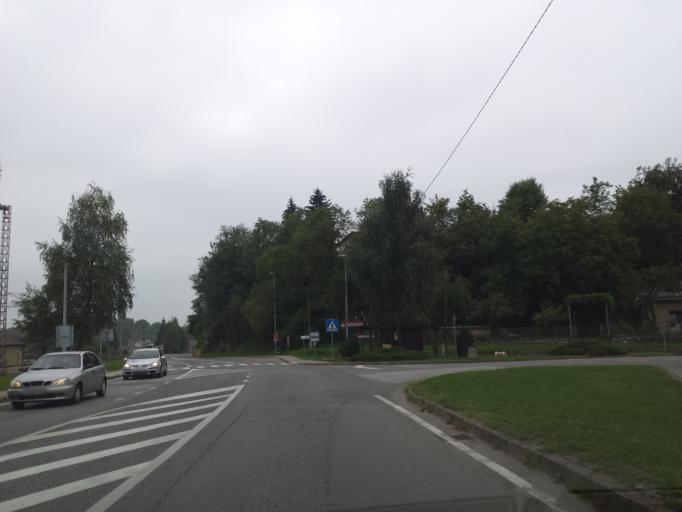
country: HR
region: Karlovacka
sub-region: Grad Karlovac
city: Karlovac
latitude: 45.4570
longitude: 15.4911
